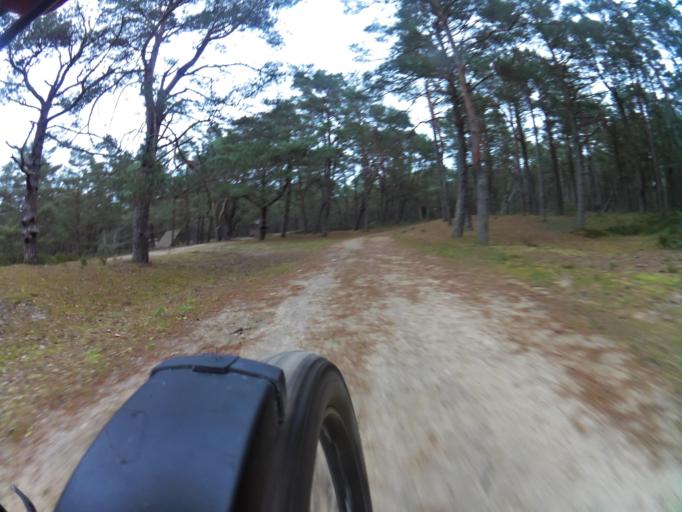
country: PL
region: Pomeranian Voivodeship
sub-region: Powiat wejherowski
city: Choczewo
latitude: 54.7827
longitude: 17.7312
